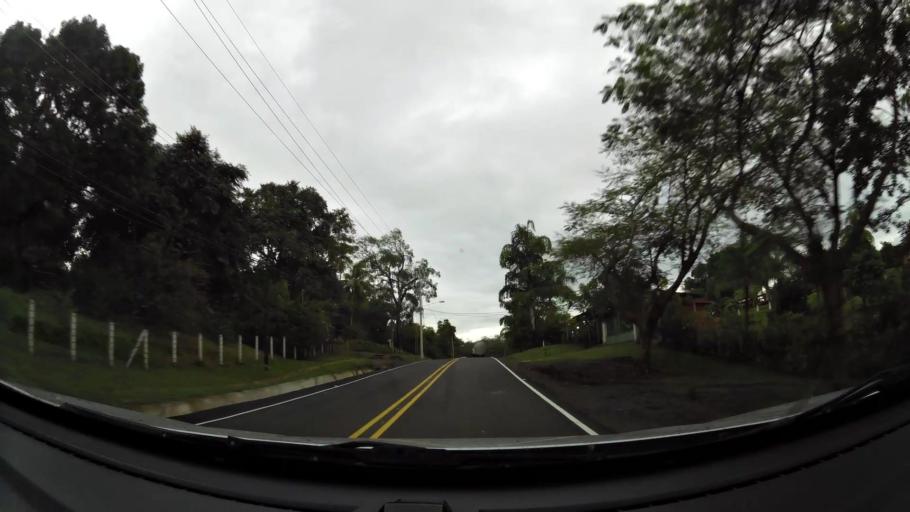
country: CR
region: Alajuela
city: Desamparados
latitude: 9.9432
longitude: -84.5418
